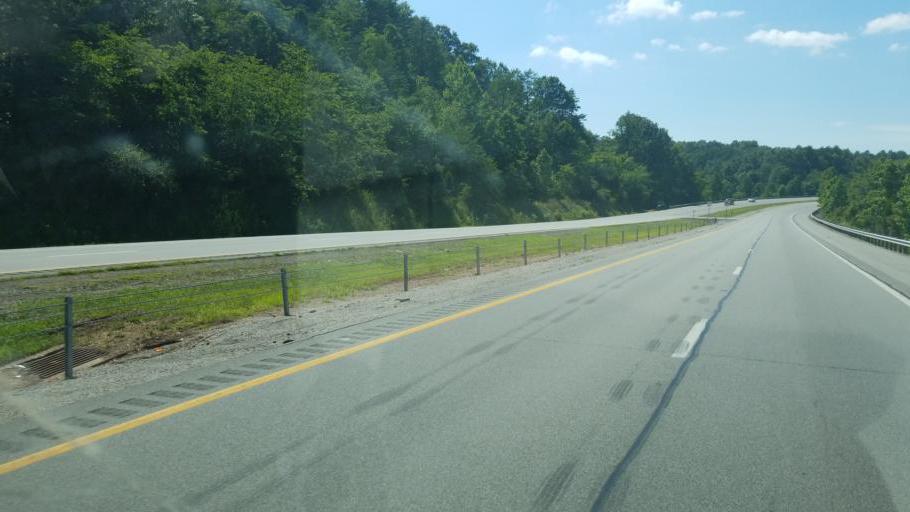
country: US
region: West Virginia
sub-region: Jackson County
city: Ripley
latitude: 38.8512
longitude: -81.7272
